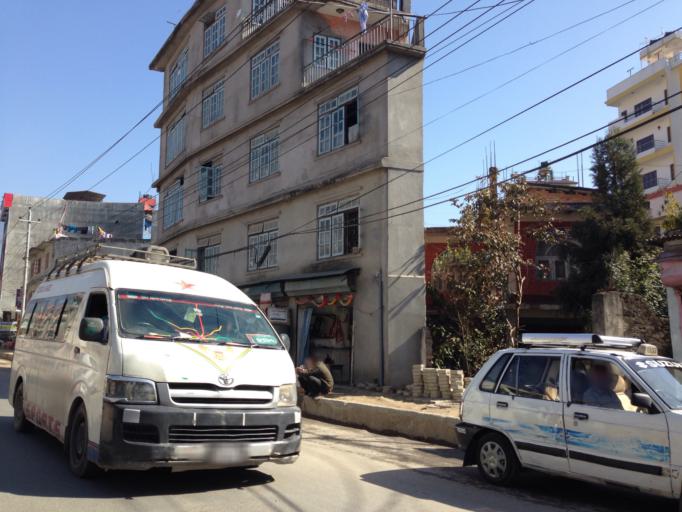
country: NP
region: Central Region
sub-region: Bagmati Zone
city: Kathmandu
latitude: 27.7569
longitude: 85.3495
